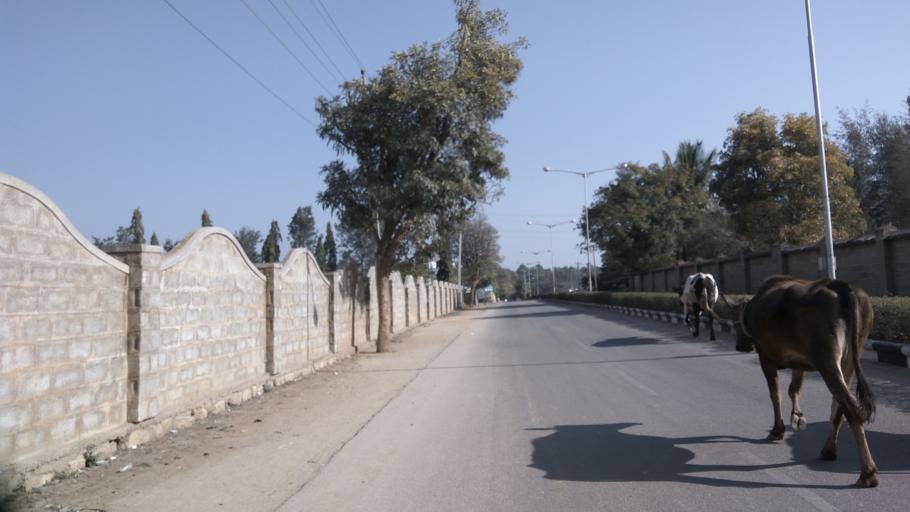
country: IN
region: Karnataka
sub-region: Bangalore Rural
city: Devanhalli
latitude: 13.2041
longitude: 77.6375
